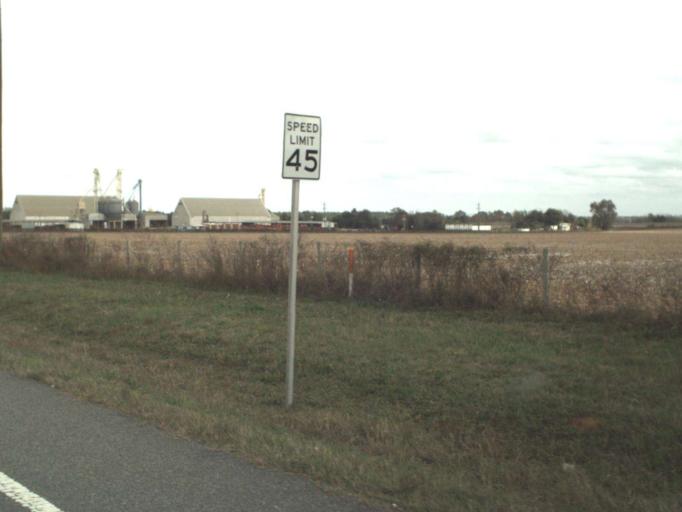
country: US
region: Florida
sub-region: Santa Rosa County
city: Point Baker
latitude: 30.7747
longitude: -87.0927
